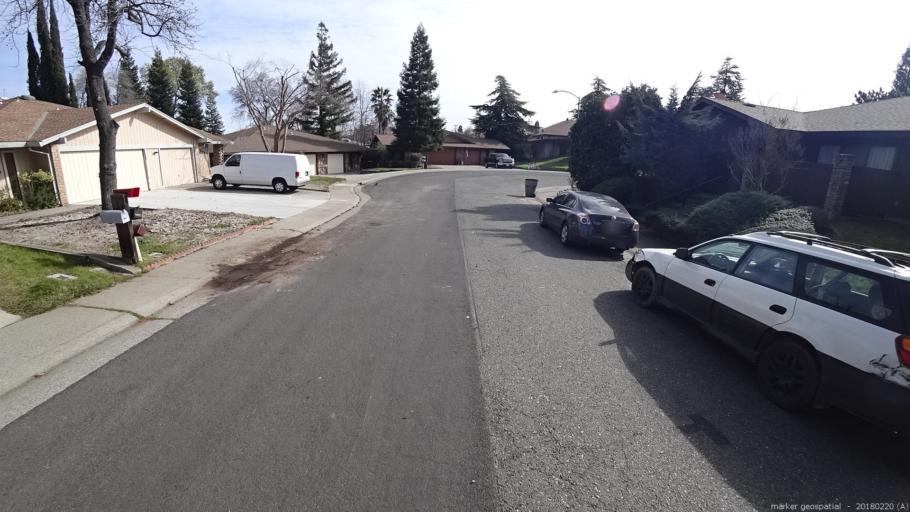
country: US
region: California
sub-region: Sacramento County
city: Orangevale
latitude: 38.6767
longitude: -121.2318
